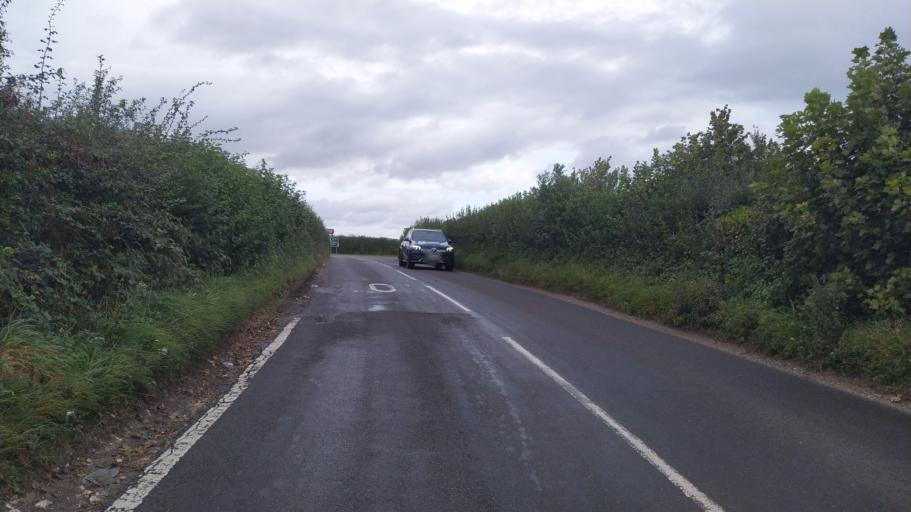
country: GB
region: England
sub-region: Dorset
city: Blandford Forum
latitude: 50.8105
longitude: -2.2044
